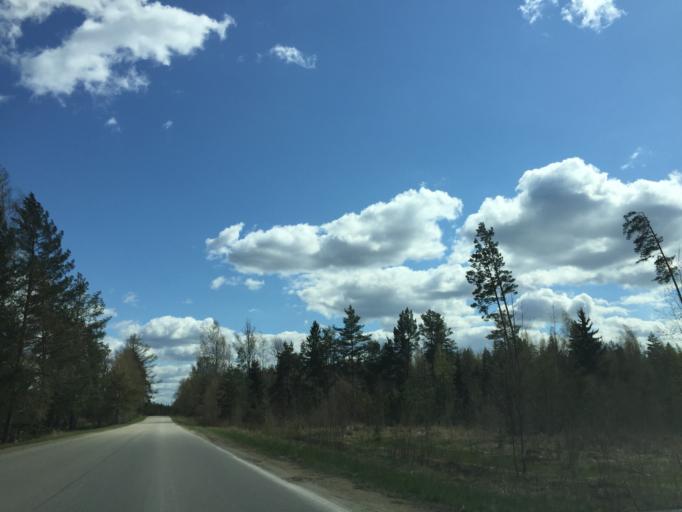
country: LV
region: Vilanu
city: Vilani
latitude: 56.5664
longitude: 27.0512
